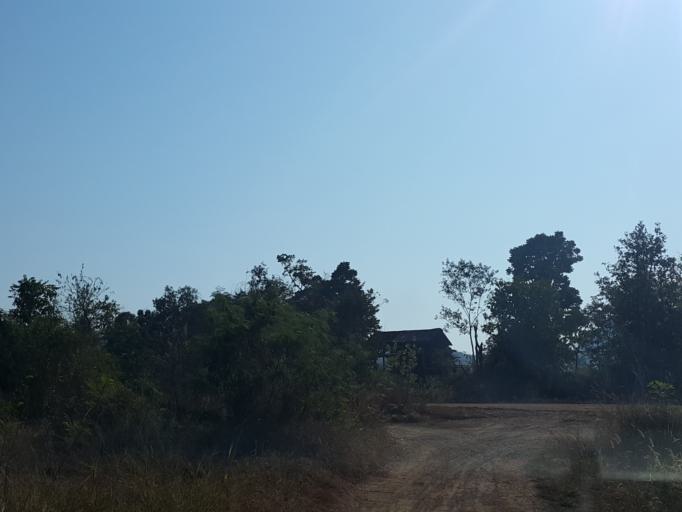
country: TH
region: Sukhothai
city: Thung Saliam
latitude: 17.3121
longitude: 99.4346
